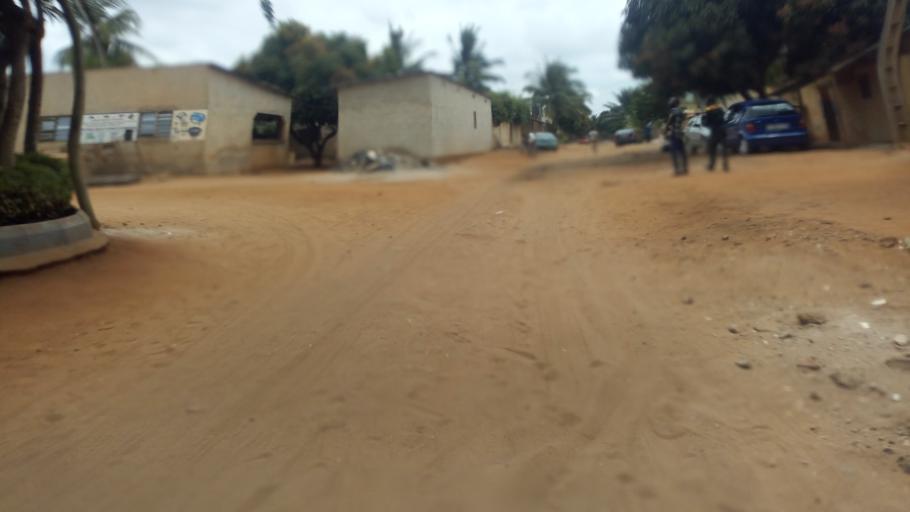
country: TG
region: Maritime
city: Lome
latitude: 6.2325
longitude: 1.1843
